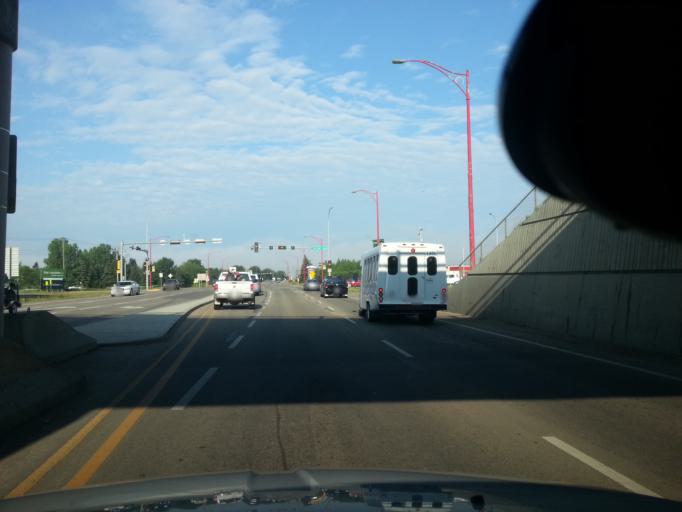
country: CA
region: Alberta
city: Leduc
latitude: 53.2649
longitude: -113.5640
